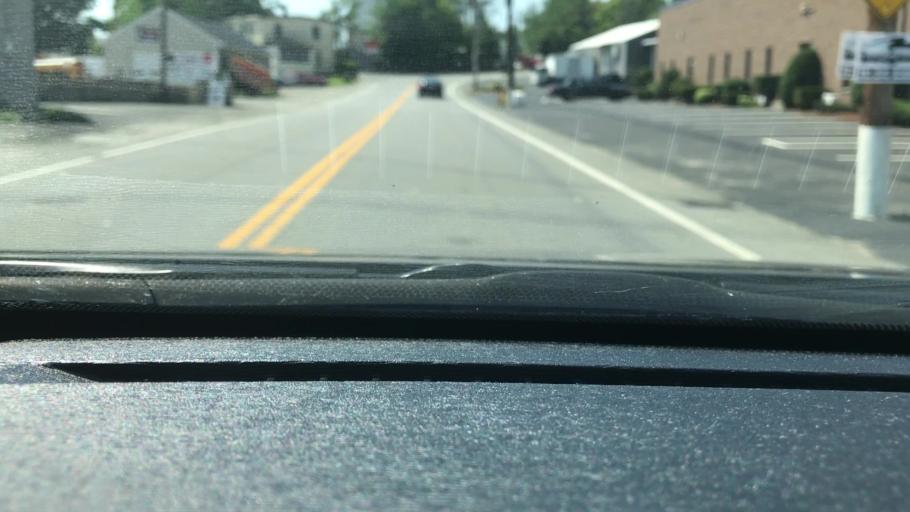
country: US
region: Massachusetts
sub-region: Middlesex County
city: Wakefield
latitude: 42.5061
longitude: -71.0645
